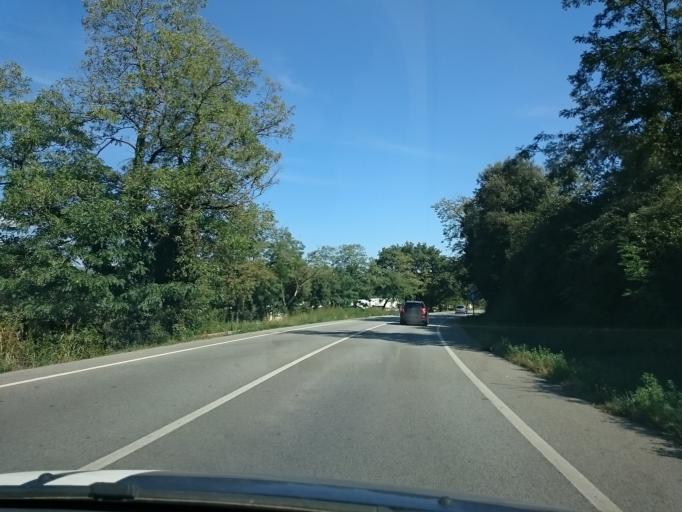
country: ES
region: Catalonia
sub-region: Provincia de Barcelona
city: Cardedeu
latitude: 41.6329
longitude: 2.3280
